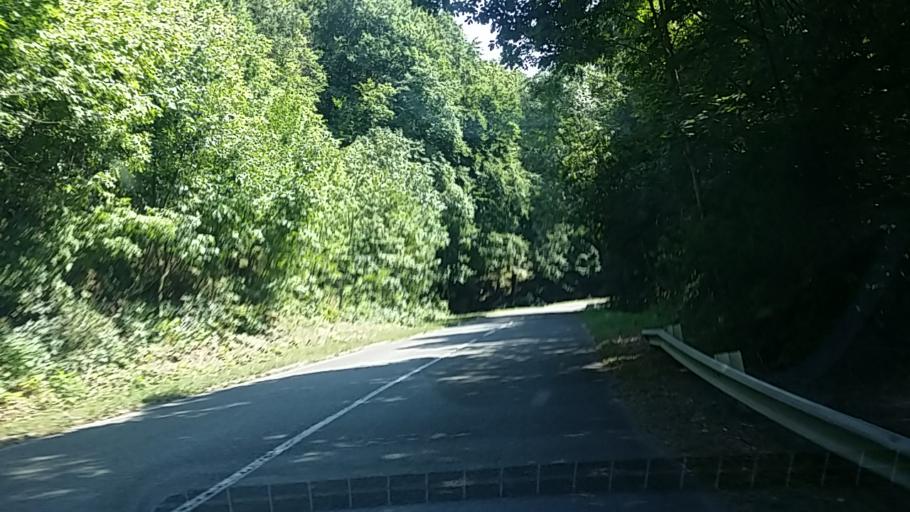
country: HU
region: Baranya
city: Pecs
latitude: 46.1163
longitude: 18.1875
